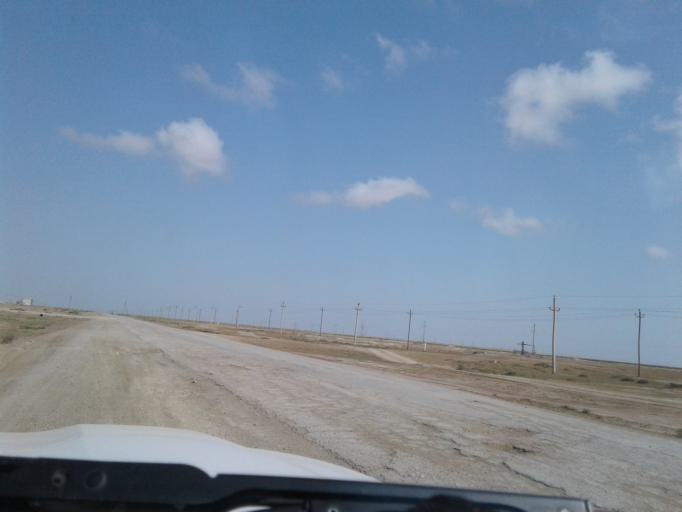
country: IR
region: Golestan
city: Gomishan
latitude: 37.7325
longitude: 53.9363
